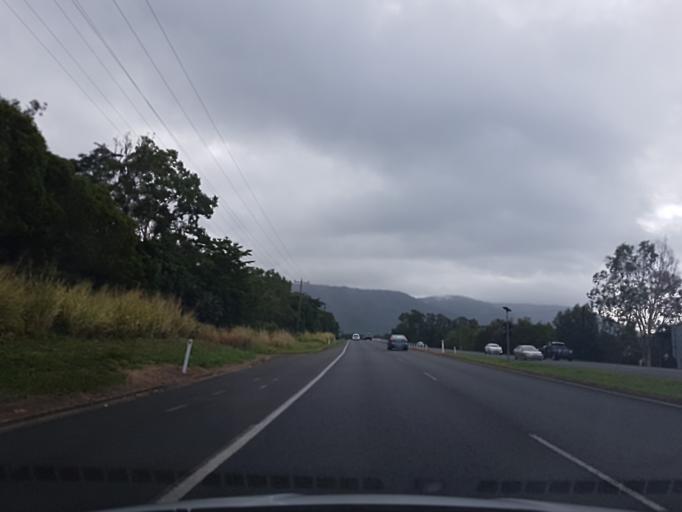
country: AU
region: Queensland
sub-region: Cairns
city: Trinity Beach
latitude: -16.7981
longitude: 145.6852
